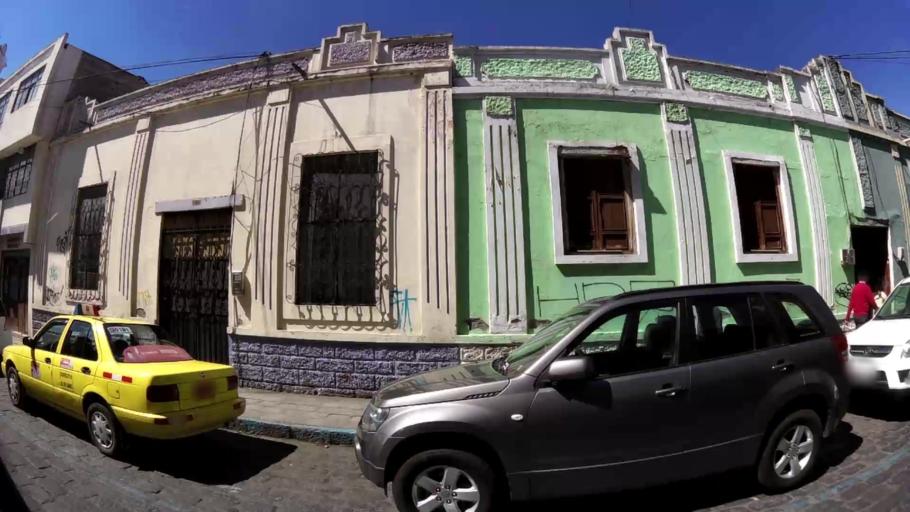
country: EC
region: Chimborazo
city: Riobamba
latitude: -1.6705
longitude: -78.6504
